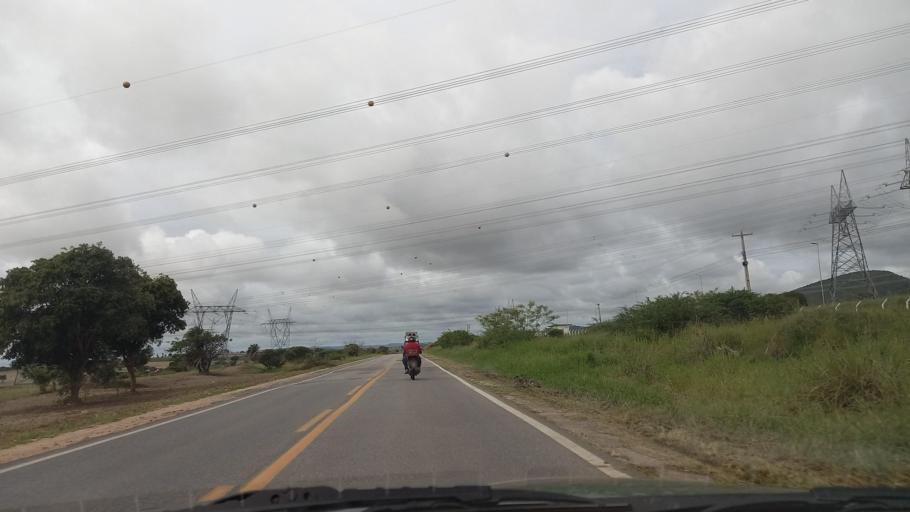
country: BR
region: Pernambuco
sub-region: Sao Joao
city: Sao Joao
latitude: -8.8803
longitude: -36.4040
